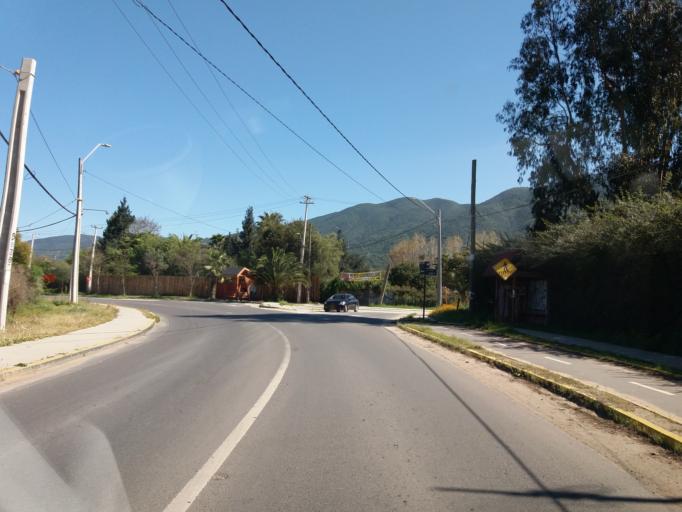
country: CL
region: Valparaiso
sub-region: Provincia de Marga Marga
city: Limache
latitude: -32.9999
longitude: -71.1783
